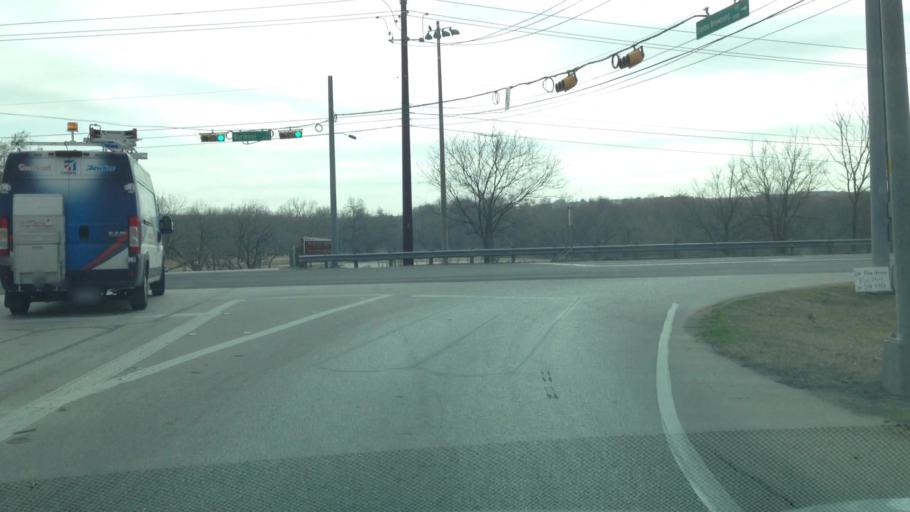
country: US
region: Texas
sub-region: Travis County
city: Garfield
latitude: 30.1734
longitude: -97.6705
